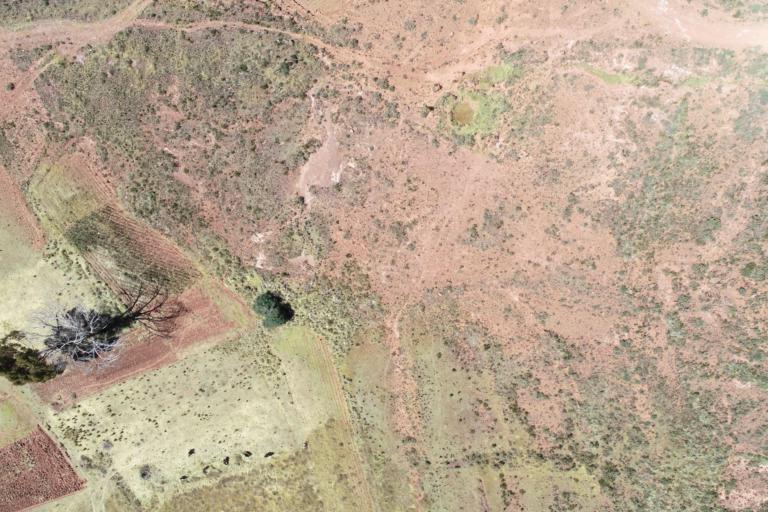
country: BO
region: La Paz
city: Tiahuanaco
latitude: -16.6040
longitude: -68.7688
